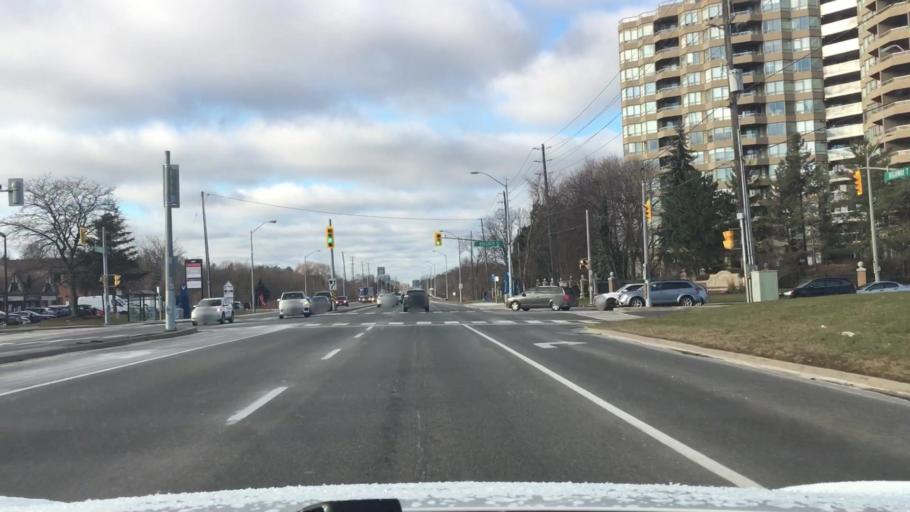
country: CA
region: Ontario
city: Markham
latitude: 43.8656
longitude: -79.2914
